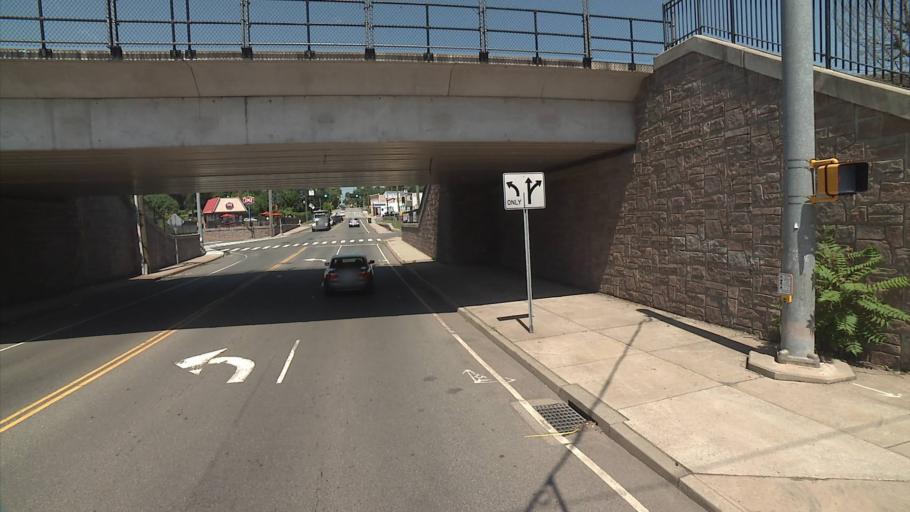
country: US
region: Connecticut
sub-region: Hartford County
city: Kensington
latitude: 41.6345
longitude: -72.7663
